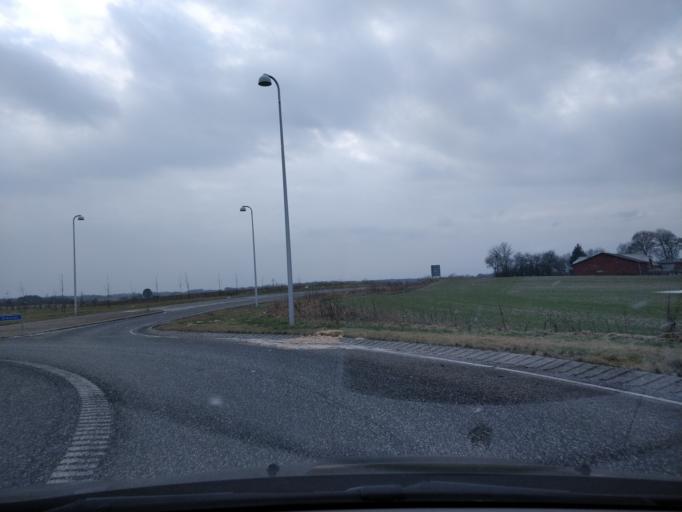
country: DK
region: South Denmark
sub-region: Vejle Kommune
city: Vejle
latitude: 55.7663
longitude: 9.5646
